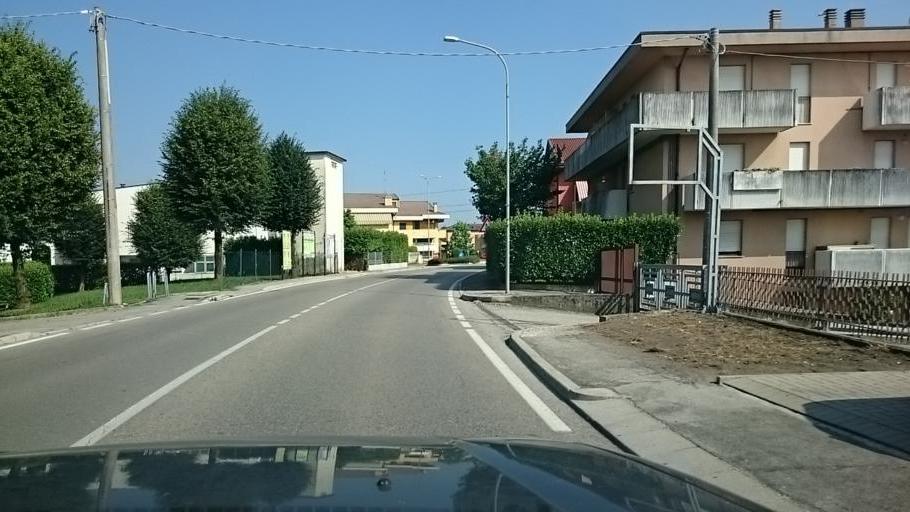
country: IT
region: Veneto
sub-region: Provincia di Padova
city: Vigodarzere
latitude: 45.4603
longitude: 11.8797
